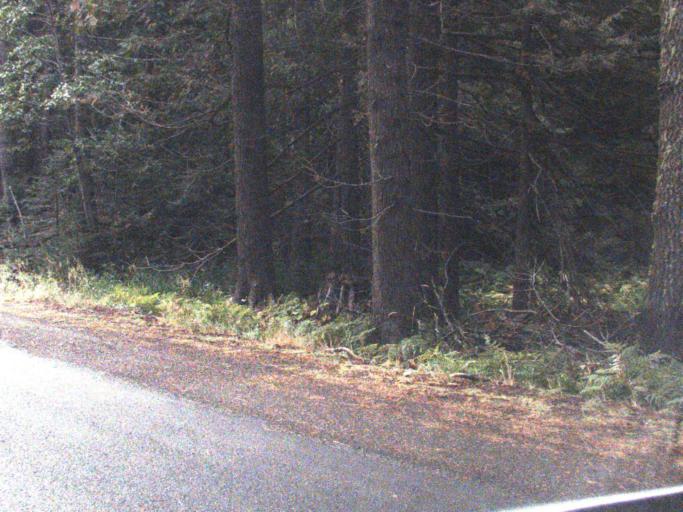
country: US
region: Washington
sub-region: Yakima County
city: Tieton
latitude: 46.6497
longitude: -121.2786
